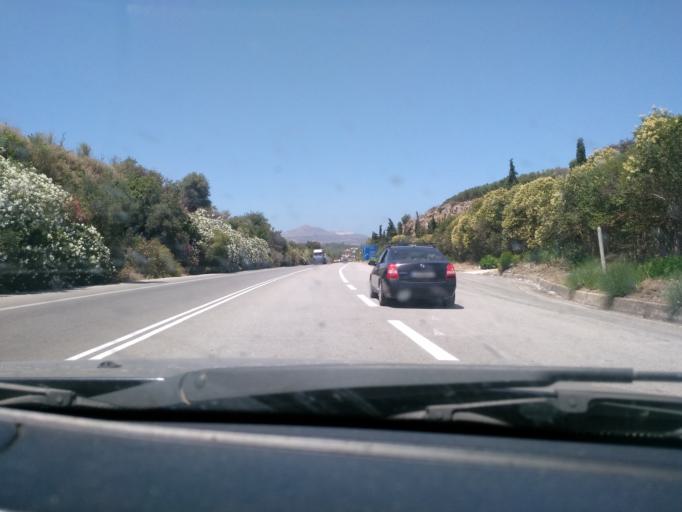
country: GR
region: Crete
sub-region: Nomos Chanias
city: Kalivai
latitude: 35.4331
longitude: 24.1658
